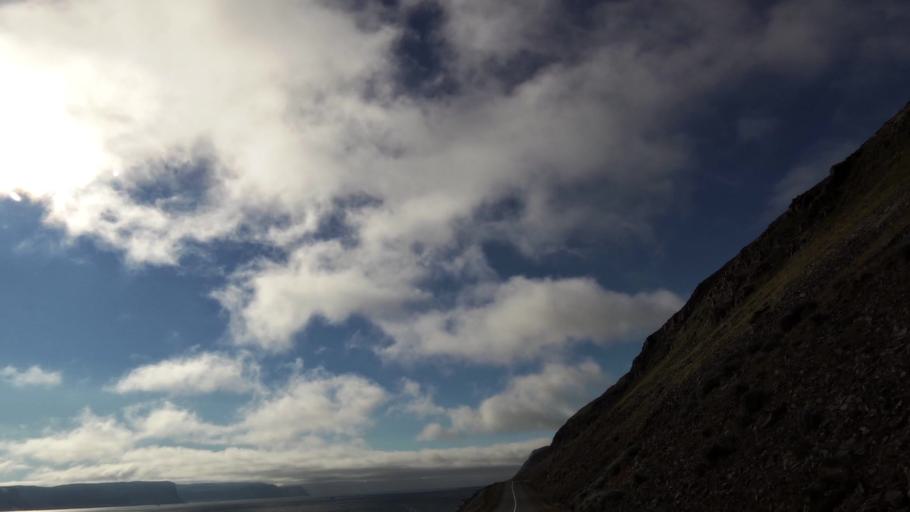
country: IS
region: West
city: Olafsvik
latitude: 65.5641
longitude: -23.9171
